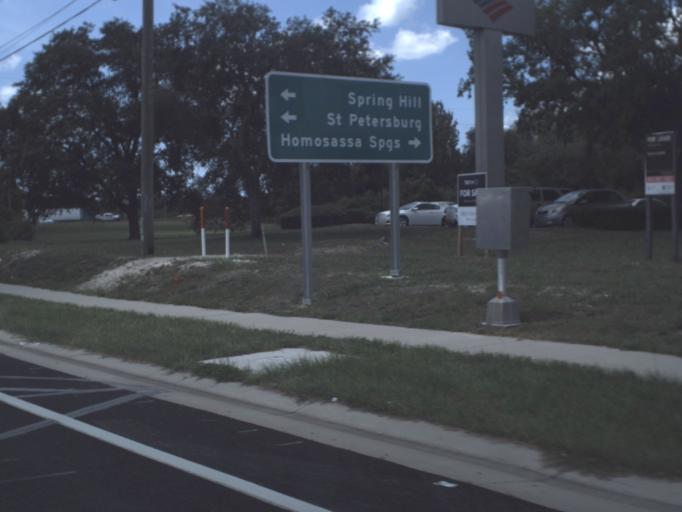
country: US
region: Florida
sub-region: Hernando County
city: North Weeki Wachee
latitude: 28.5192
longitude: -82.5685
